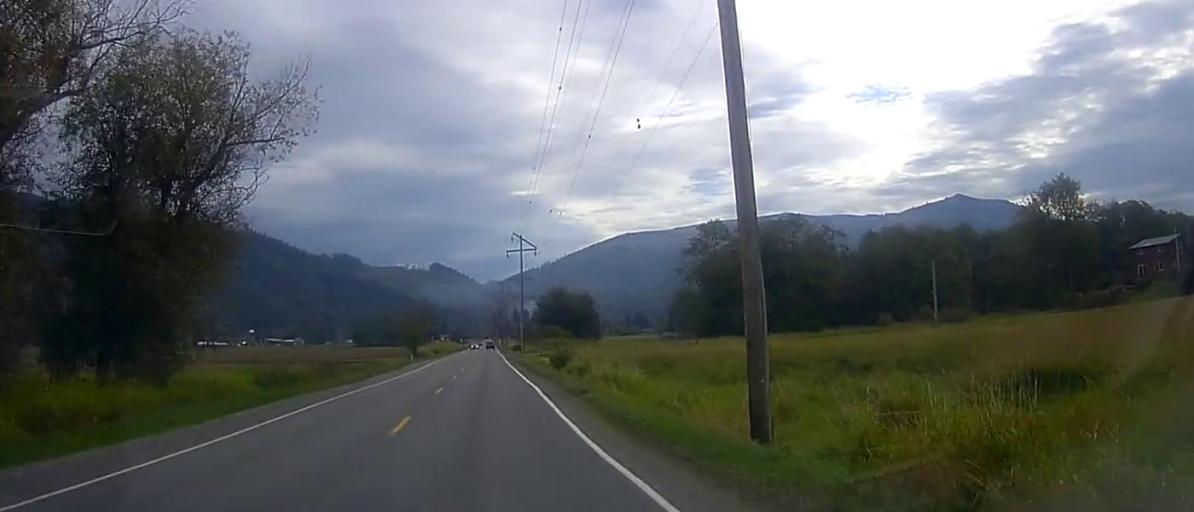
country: US
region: Washington
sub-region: Skagit County
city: Clear Lake
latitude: 48.4679
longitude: -122.2494
